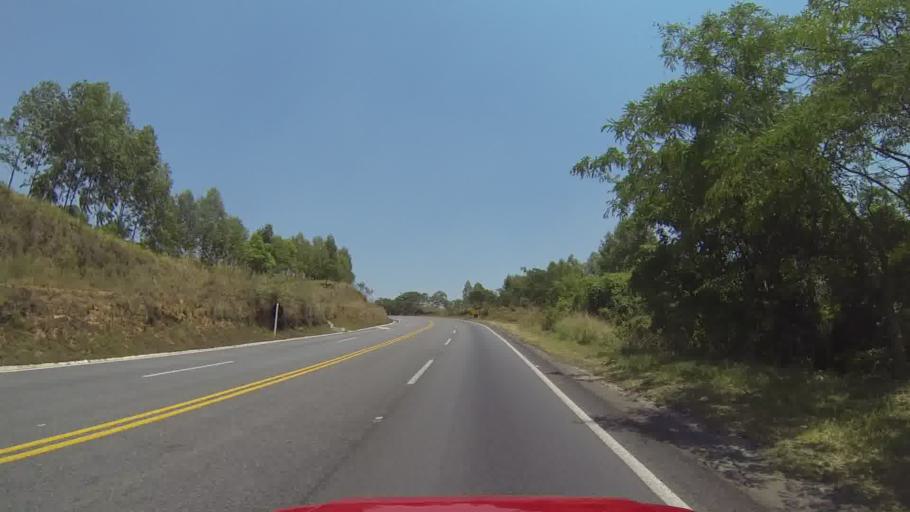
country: BR
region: Minas Gerais
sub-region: Itapecerica
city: Itapecerica
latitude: -20.2679
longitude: -45.1152
